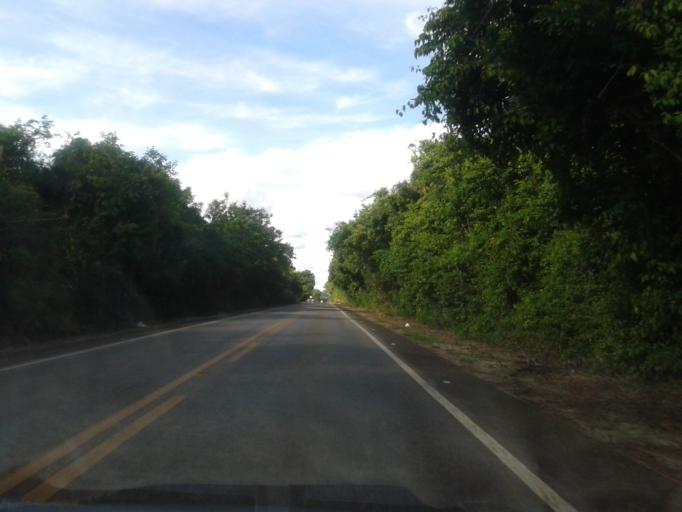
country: BR
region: Goias
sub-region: Mozarlandia
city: Mozarlandia
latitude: -14.5964
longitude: -50.5100
